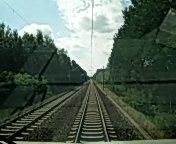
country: DE
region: Brandenburg
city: Halbe
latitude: 52.0522
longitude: 13.7208
